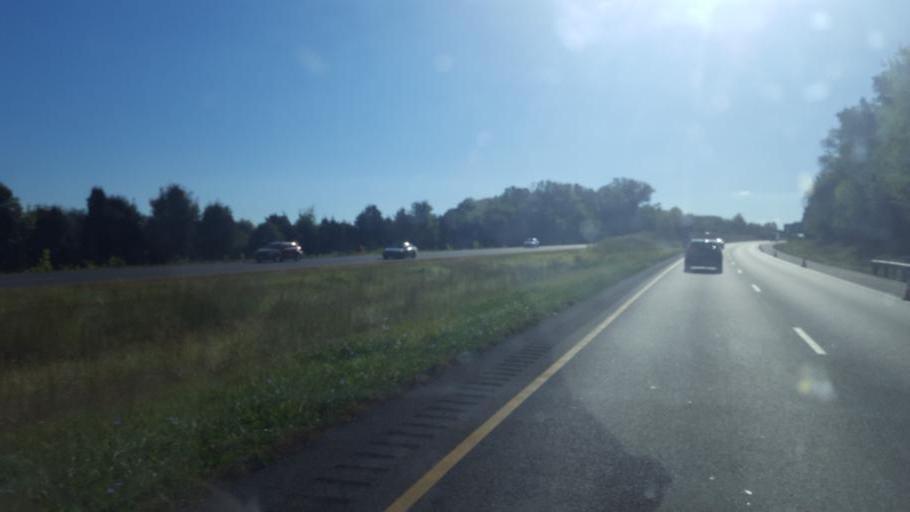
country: US
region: Maryland
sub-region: Washington County
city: Wilson-Conococheague
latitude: 39.6369
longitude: -77.8209
